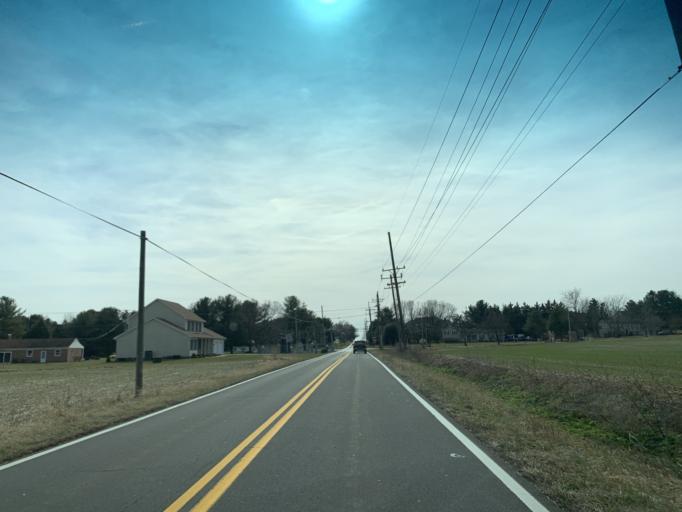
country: US
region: Maryland
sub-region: Frederick County
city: Adamstown
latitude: 39.3139
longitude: -77.4602
